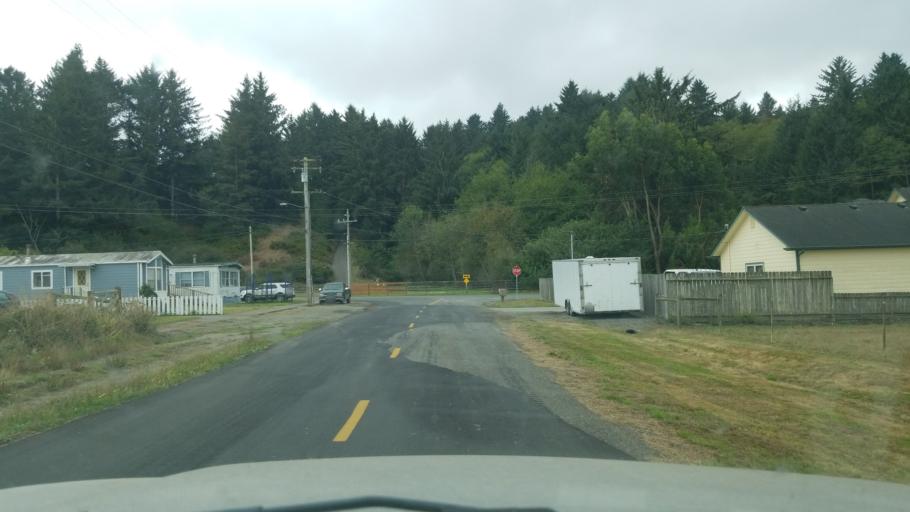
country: US
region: California
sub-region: Humboldt County
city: Ferndale
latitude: 40.5822
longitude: -124.2838
